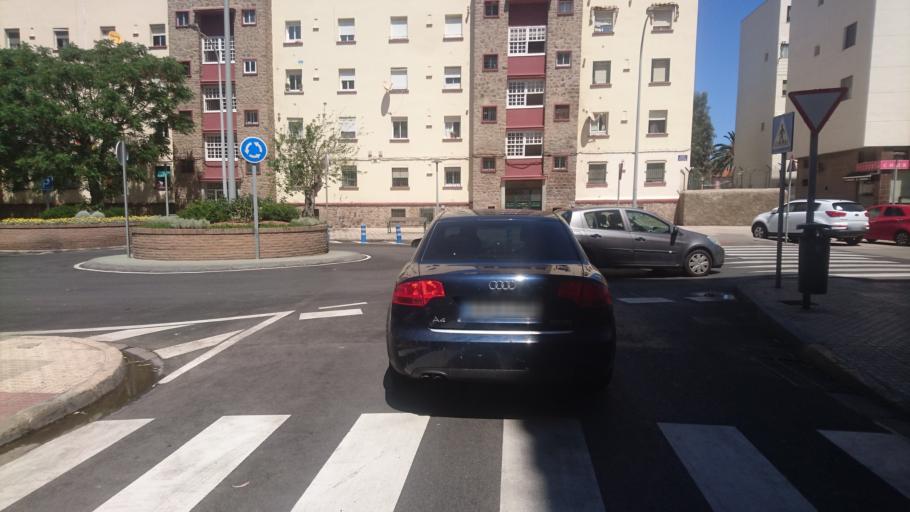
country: ES
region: Melilla
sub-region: Melilla
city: Melilla
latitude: 35.2755
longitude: -2.9389
